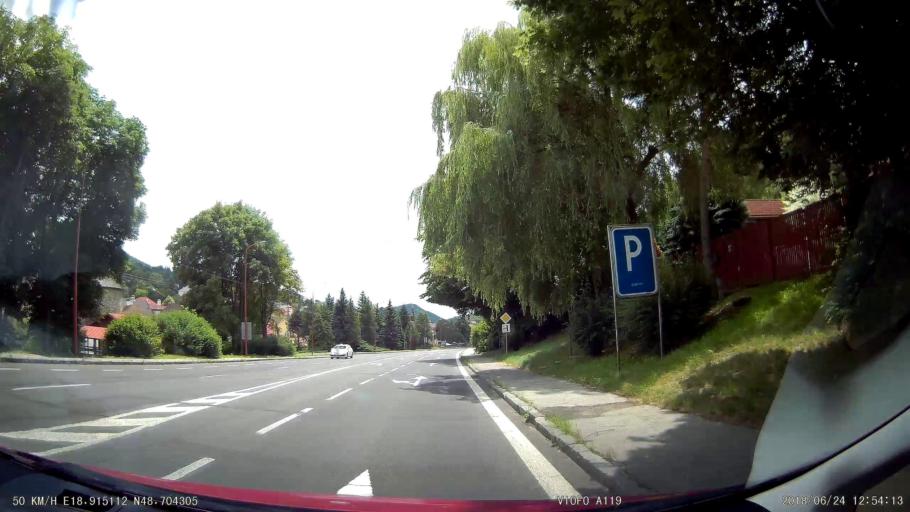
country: SK
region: Banskobystricky
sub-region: Okres Ziar nad Hronom
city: Kremnica
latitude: 48.7043
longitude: 18.9151
